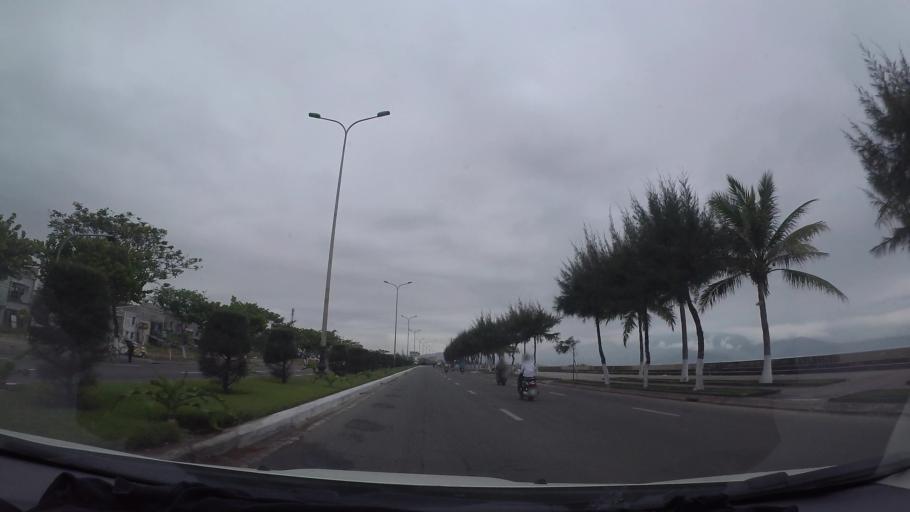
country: VN
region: Da Nang
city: Lien Chieu
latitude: 16.0835
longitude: 108.1626
